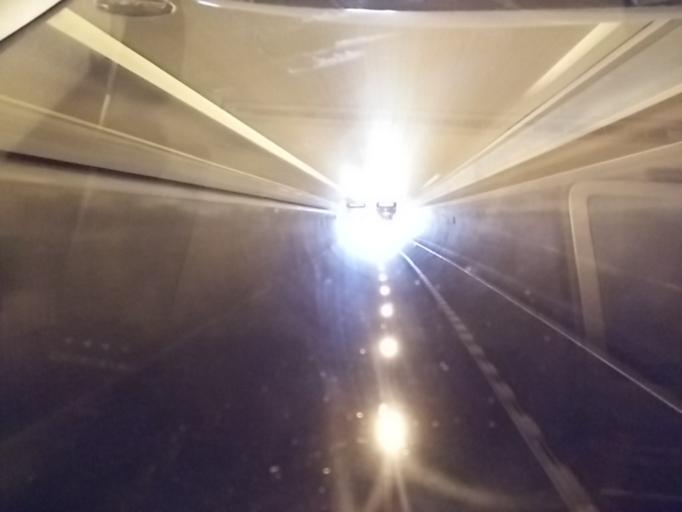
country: DE
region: Baden-Wuerttemberg
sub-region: Regierungsbezirk Stuttgart
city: Nufringen
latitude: 48.6061
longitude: 8.8972
